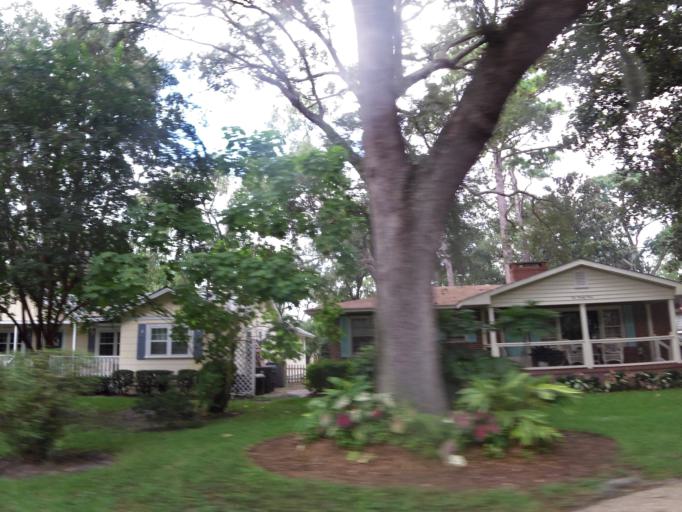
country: US
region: Georgia
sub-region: Glynn County
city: Saint Simons Island
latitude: 31.1372
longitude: -81.3908
